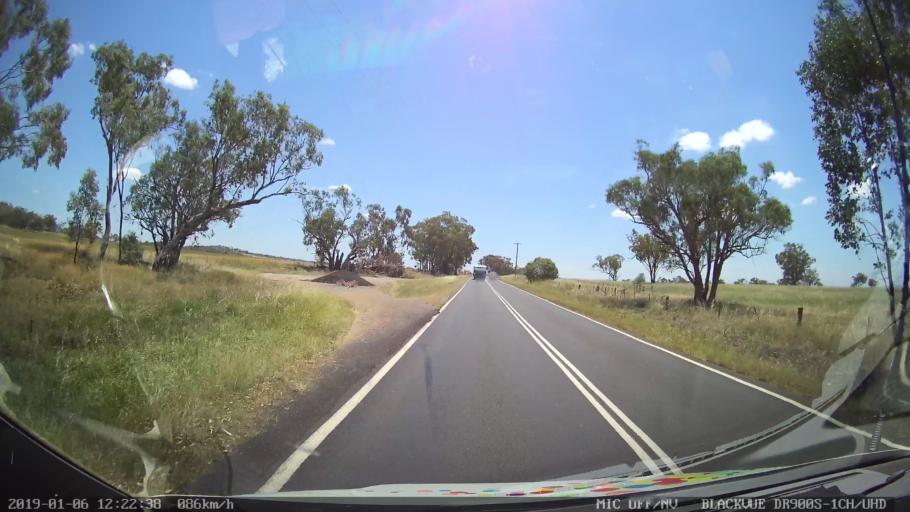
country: AU
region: New South Wales
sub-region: Tamworth Municipality
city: Phillip
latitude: -31.2597
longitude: 150.7890
